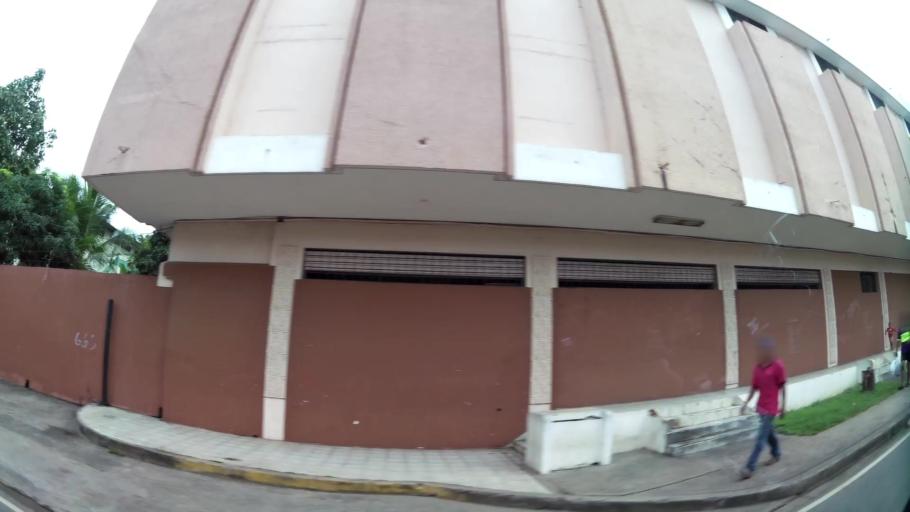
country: PA
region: Panama
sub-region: Distrito de Panama
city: Ancon
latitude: 8.9712
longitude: -79.5406
